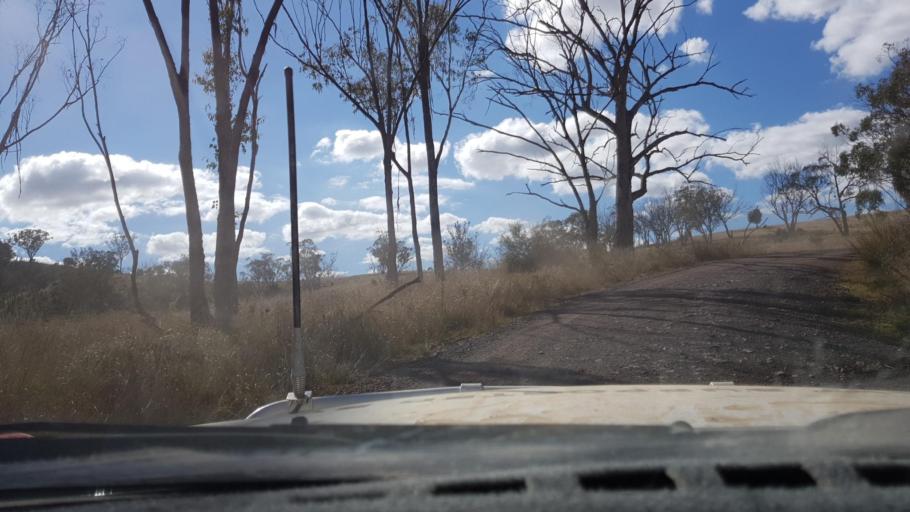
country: AU
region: New South Wales
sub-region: Tamworth Municipality
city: Manilla
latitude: -30.4717
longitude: 150.7738
